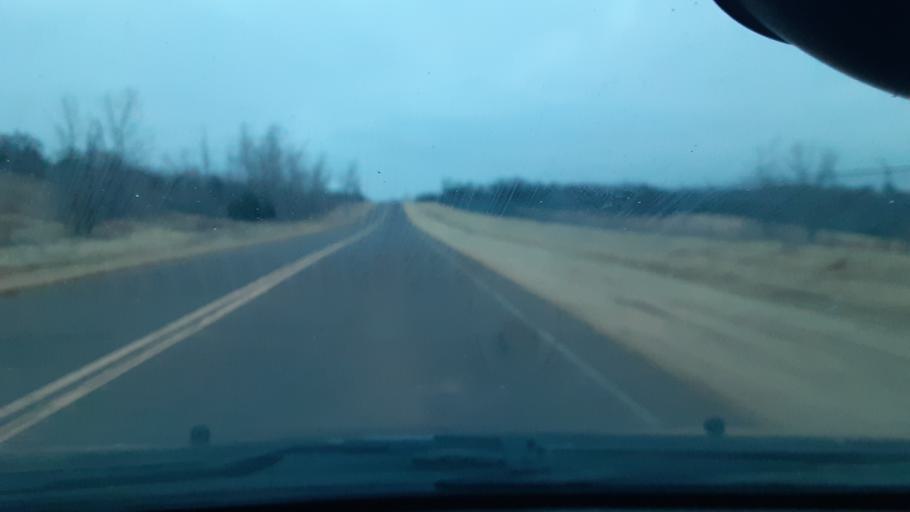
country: US
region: Oklahoma
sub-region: Logan County
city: Guthrie
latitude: 35.8604
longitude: -97.4157
